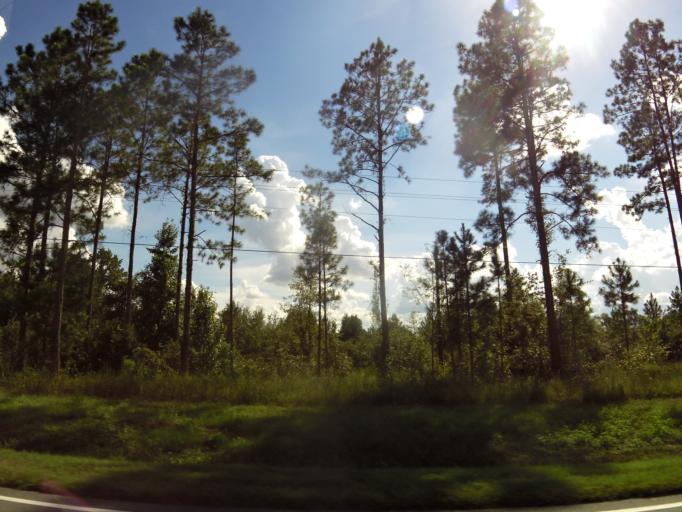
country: US
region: Georgia
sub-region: Lowndes County
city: Valdosta
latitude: 30.8056
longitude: -83.2074
